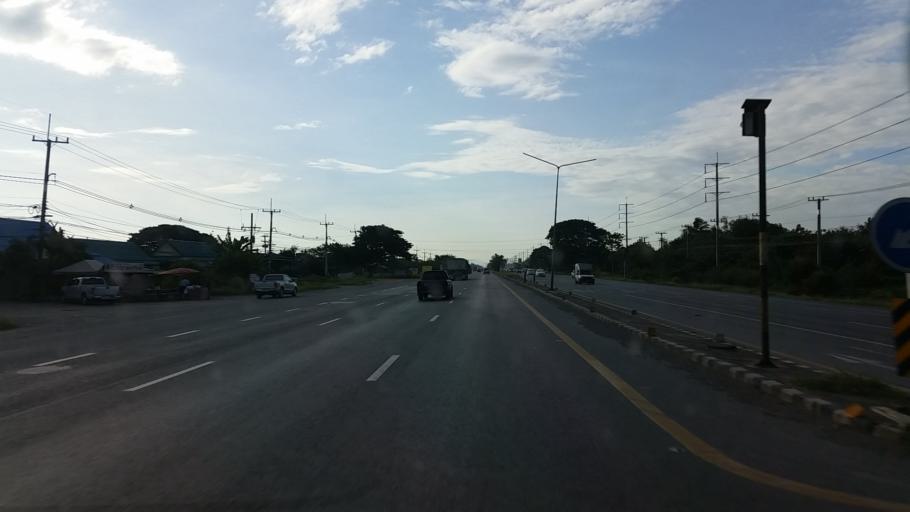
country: TH
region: Sara Buri
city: Chaloem Phra Kiat
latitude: 14.6157
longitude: 100.8925
